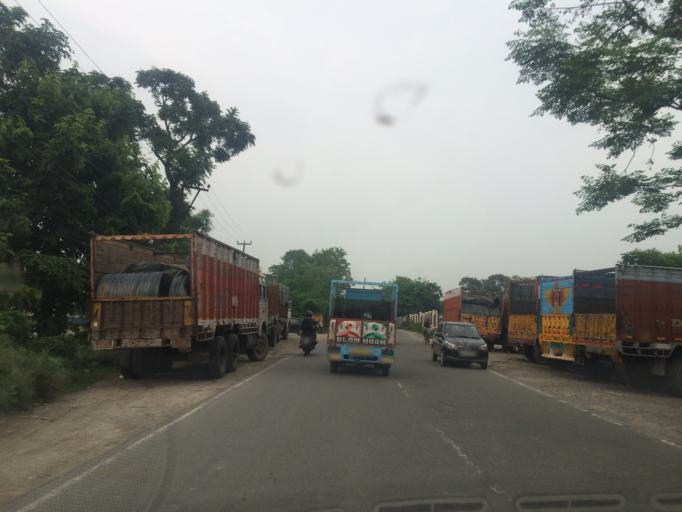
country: IN
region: Uttarakhand
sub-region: Dehradun
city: Doiwala
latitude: 30.1774
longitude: 78.1284
